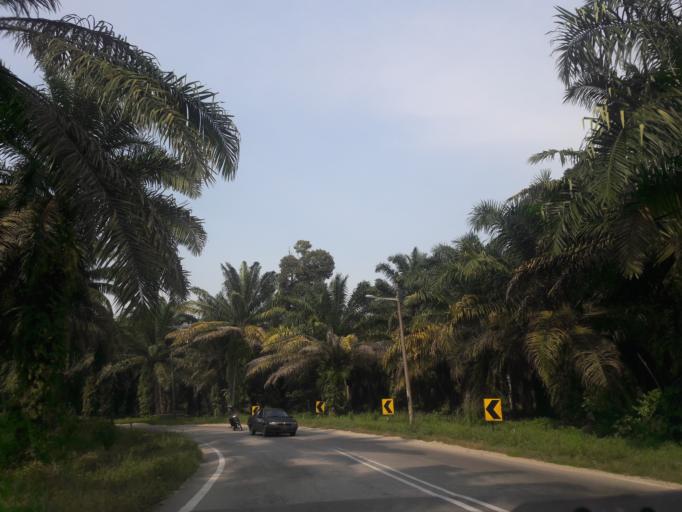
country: MY
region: Kedah
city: Kulim
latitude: 5.3621
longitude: 100.5214
